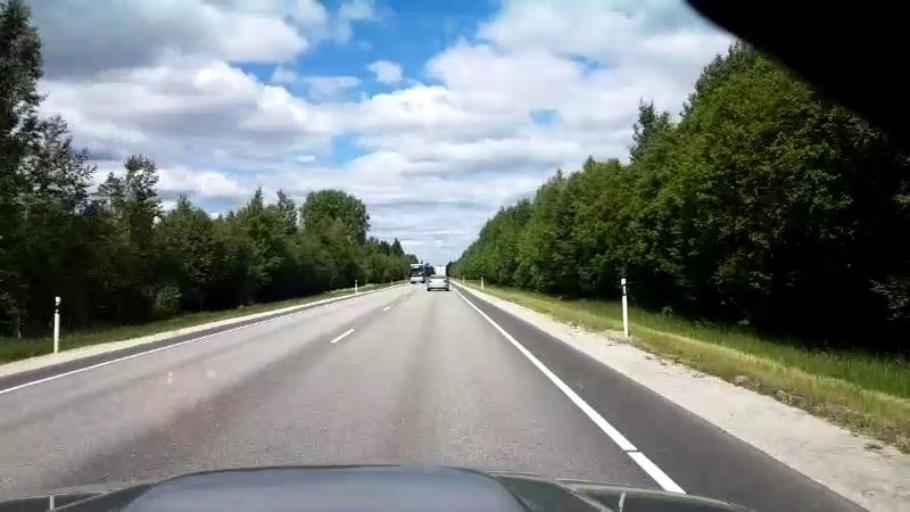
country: EE
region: Paernumaa
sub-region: Halinga vald
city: Parnu-Jaagupi
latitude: 58.7132
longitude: 24.4239
